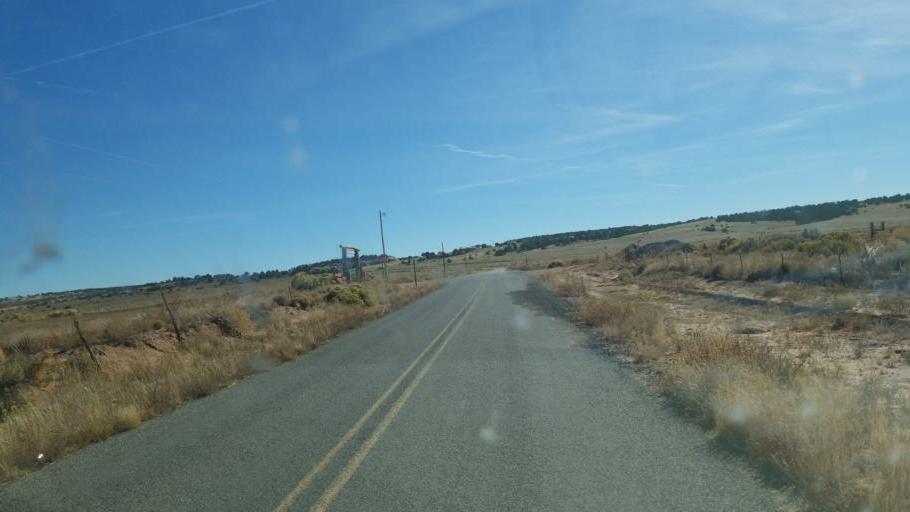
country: US
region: New Mexico
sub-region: McKinley County
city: Thoreau
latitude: 35.4460
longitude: -108.0520
